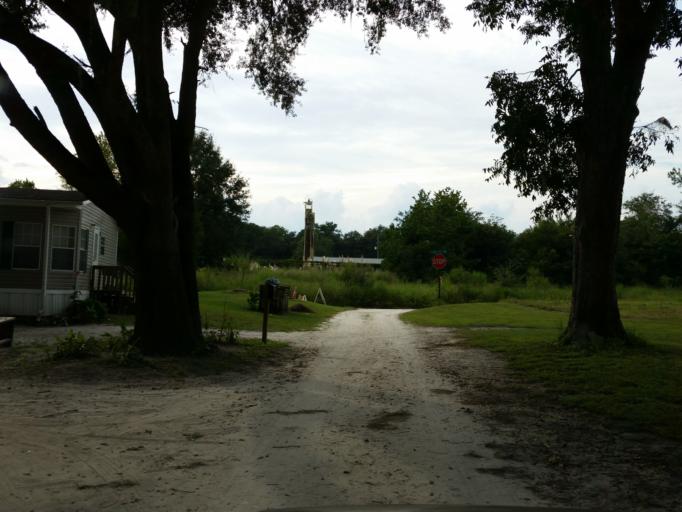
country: US
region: Florida
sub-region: Suwannee County
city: Live Oak
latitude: 30.3034
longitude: -82.9836
